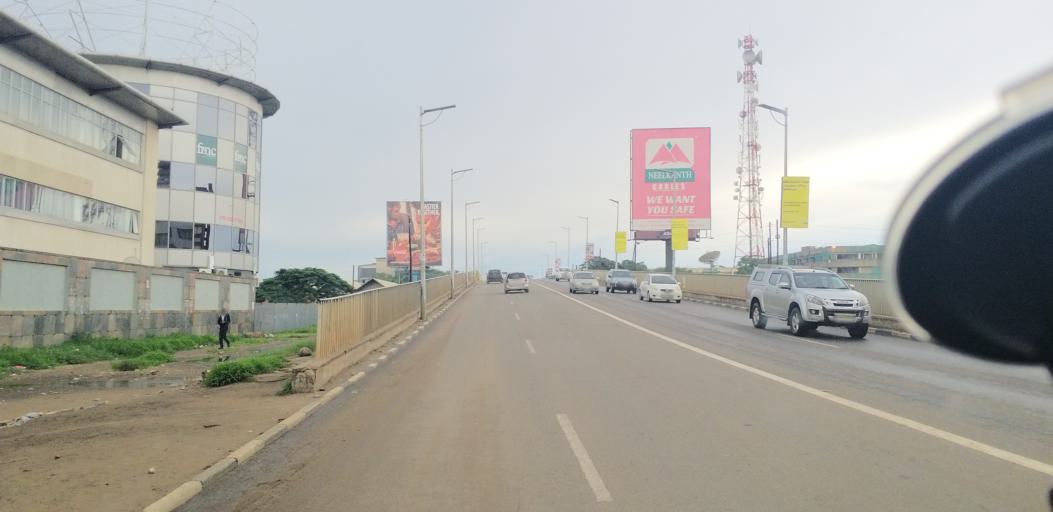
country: ZM
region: Lusaka
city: Lusaka
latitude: -15.4161
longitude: 28.2821
